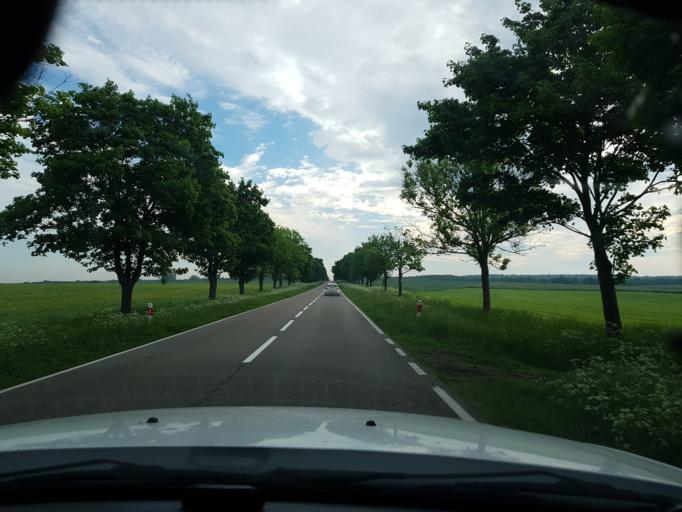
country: PL
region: West Pomeranian Voivodeship
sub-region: Powiat stargardzki
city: Stara Dabrowa
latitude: 53.3870
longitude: 15.1828
